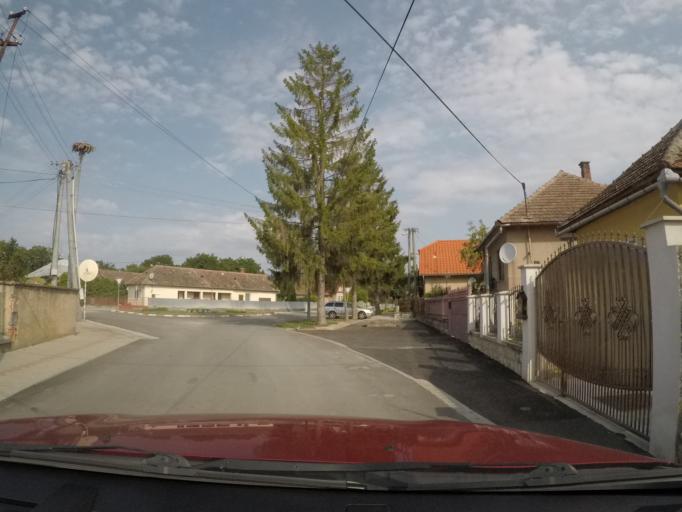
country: SK
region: Kosicky
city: Moldava nad Bodvou
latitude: 48.5874
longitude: 20.9953
